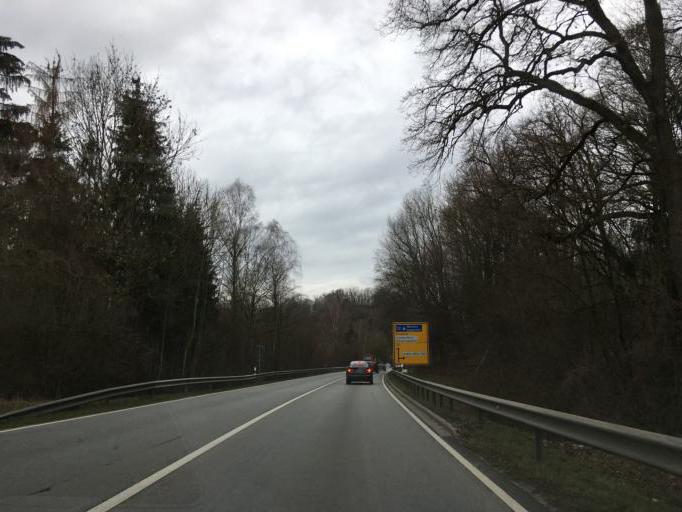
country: DE
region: Bavaria
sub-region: Lower Bavaria
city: Landau an der Isar
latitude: 48.6623
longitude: 12.6877
